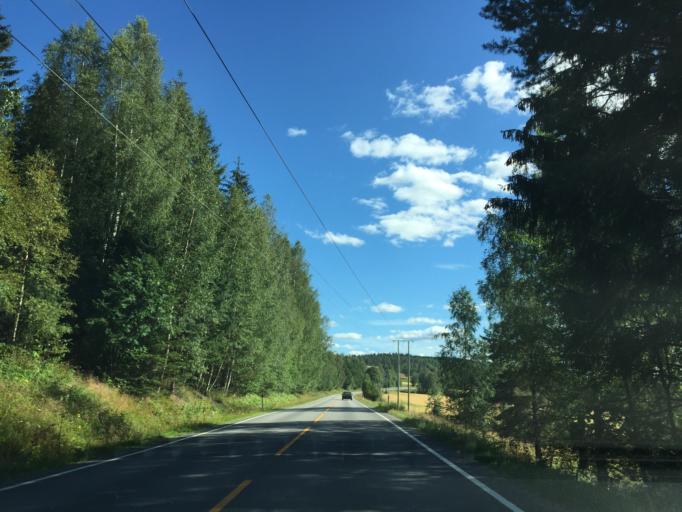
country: NO
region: Hedmark
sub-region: Sor-Odal
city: Skarnes
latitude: 60.2308
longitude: 11.6788
